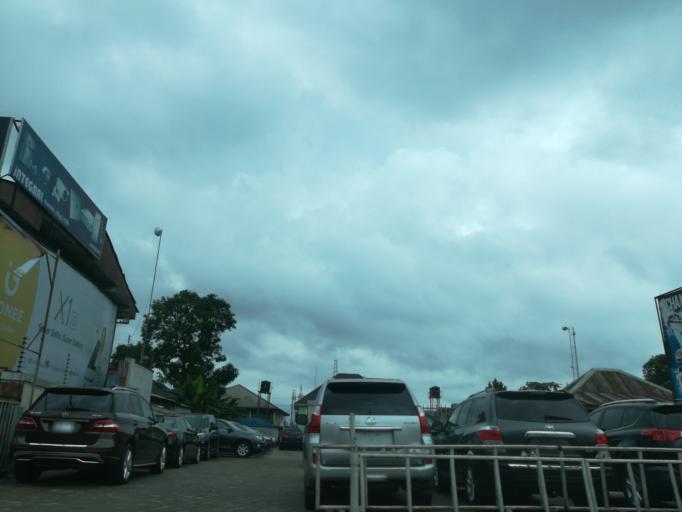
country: NG
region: Rivers
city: Port Harcourt
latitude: 4.8356
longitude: 7.0277
